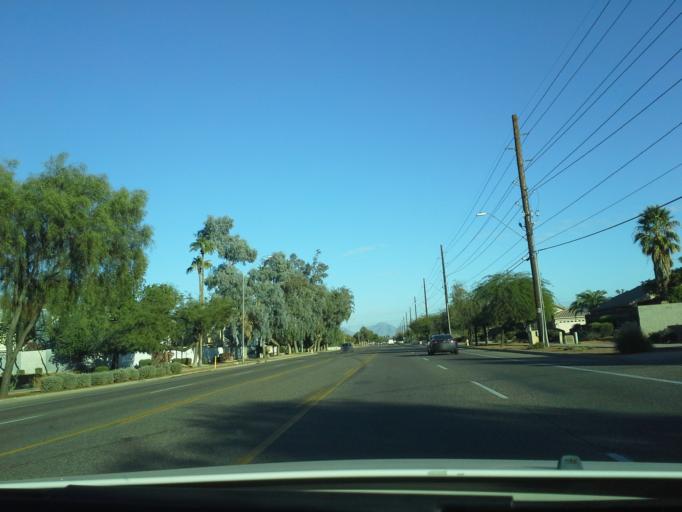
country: US
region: Arizona
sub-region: Maricopa County
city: Glendale
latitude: 33.6546
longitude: -112.0813
